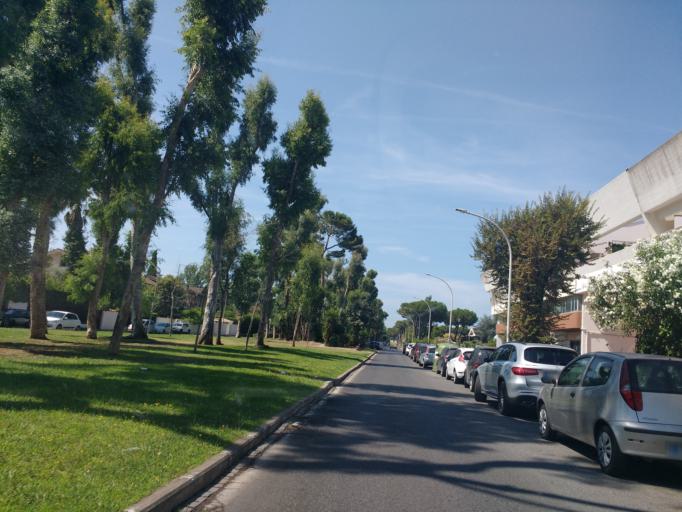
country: IT
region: Latium
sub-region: Citta metropolitana di Roma Capitale
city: Acilia-Castel Fusano-Ostia Antica
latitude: 41.7533
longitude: 12.3586
